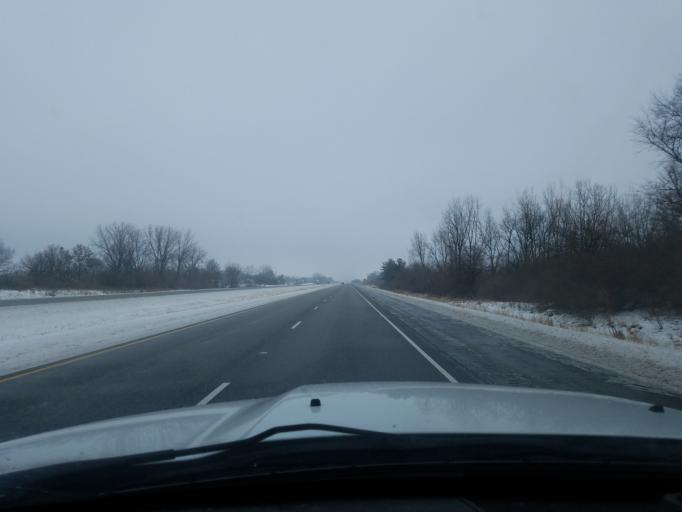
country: US
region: Indiana
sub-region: Fulton County
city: Rochester
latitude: 40.9541
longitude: -86.1683
